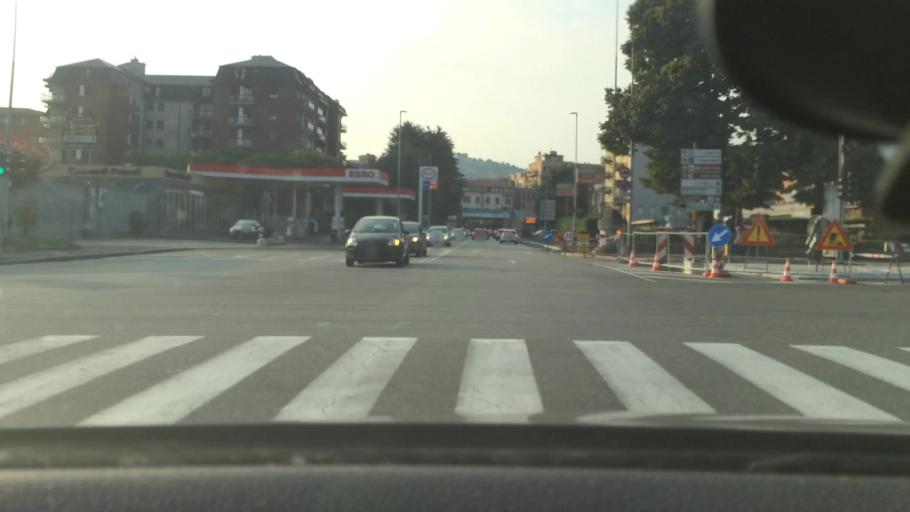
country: IT
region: Lombardy
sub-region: Provincia di Bergamo
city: Bergamo
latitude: 45.6859
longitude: 9.6689
